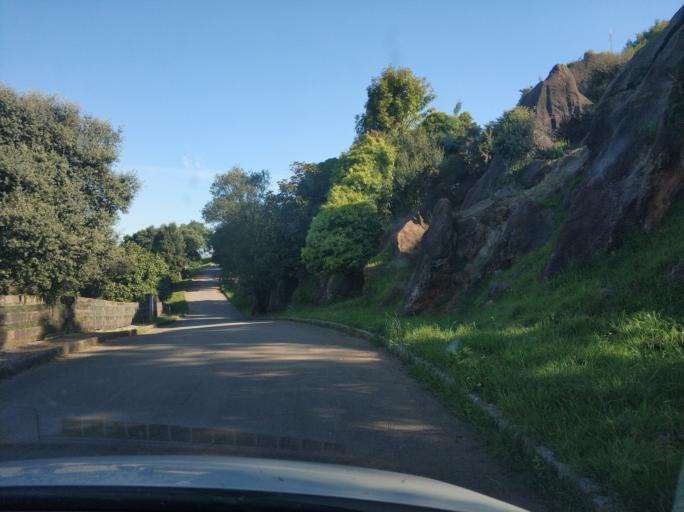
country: ES
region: Cantabria
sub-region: Provincia de Cantabria
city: Santa Maria de Cayon
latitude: 43.3443
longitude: -3.8565
